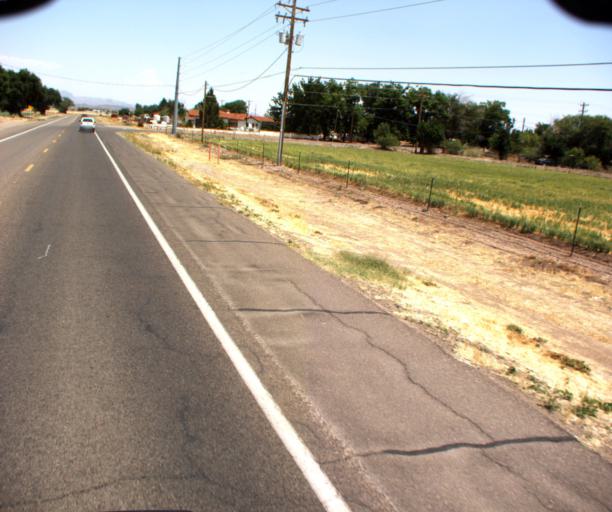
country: US
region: Arizona
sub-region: Graham County
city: Safford
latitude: 32.8166
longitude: -109.6360
